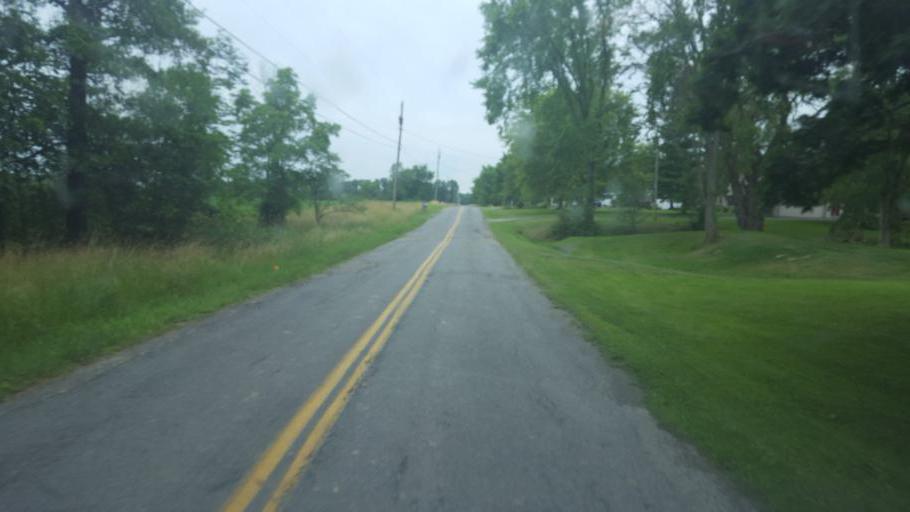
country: US
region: Ohio
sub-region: Trumbull County
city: South Canal
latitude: 41.1810
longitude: -81.0233
